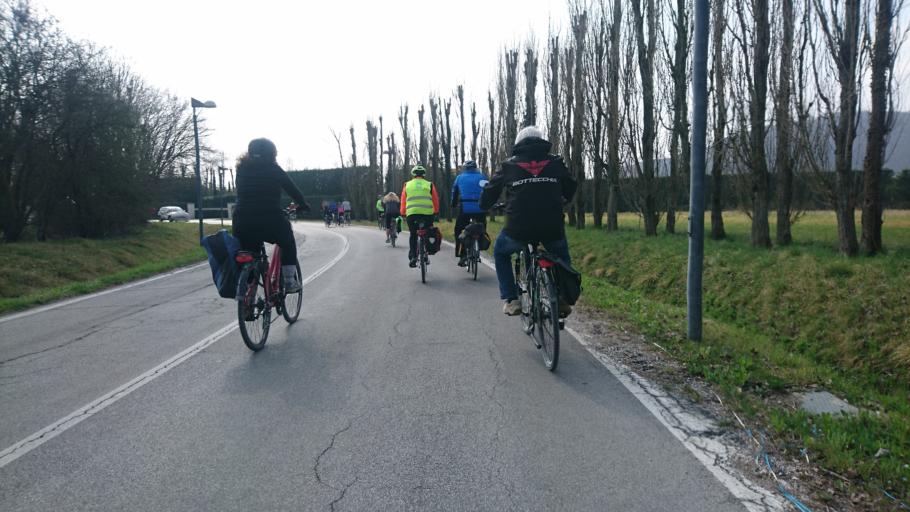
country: IT
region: Veneto
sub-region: Provincia di Padova
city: Abano Terme
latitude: 45.3632
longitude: 11.7612
